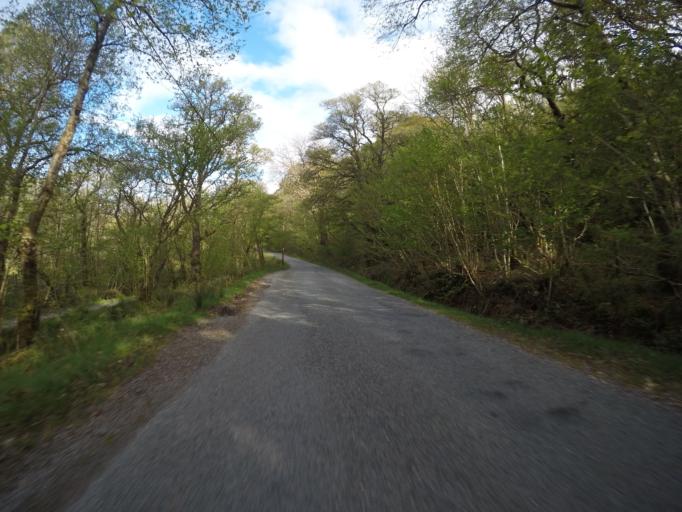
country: GB
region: Scotland
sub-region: Highland
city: Fort William
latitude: 56.6758
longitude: -5.0772
